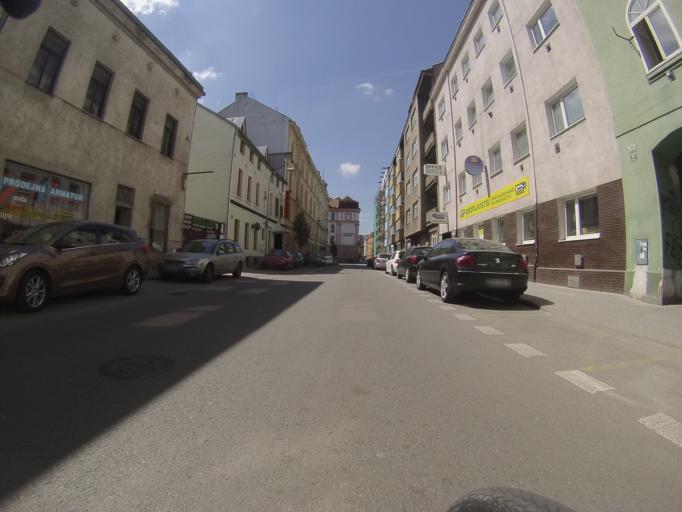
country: CZ
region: South Moravian
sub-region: Mesto Brno
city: Brno
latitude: 49.1924
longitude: 16.6207
